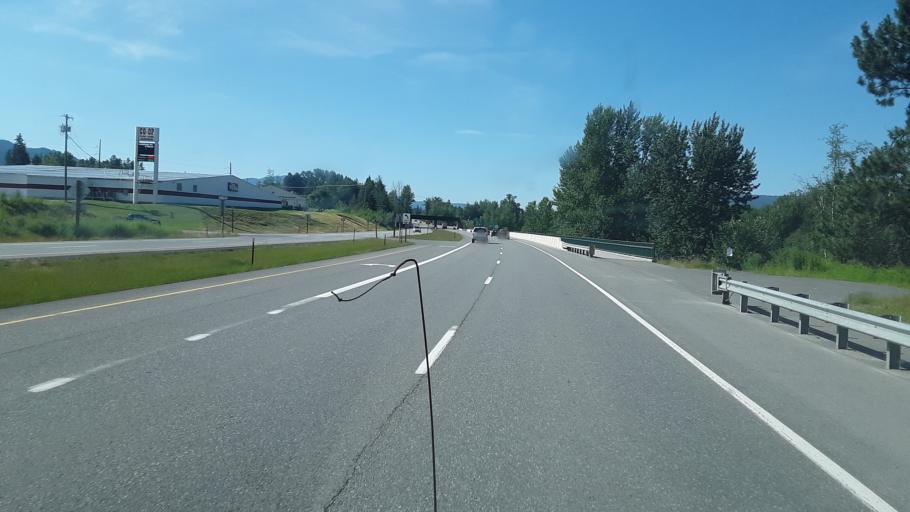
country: US
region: Idaho
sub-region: Bonner County
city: Ponderay
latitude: 48.2985
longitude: -116.5481
